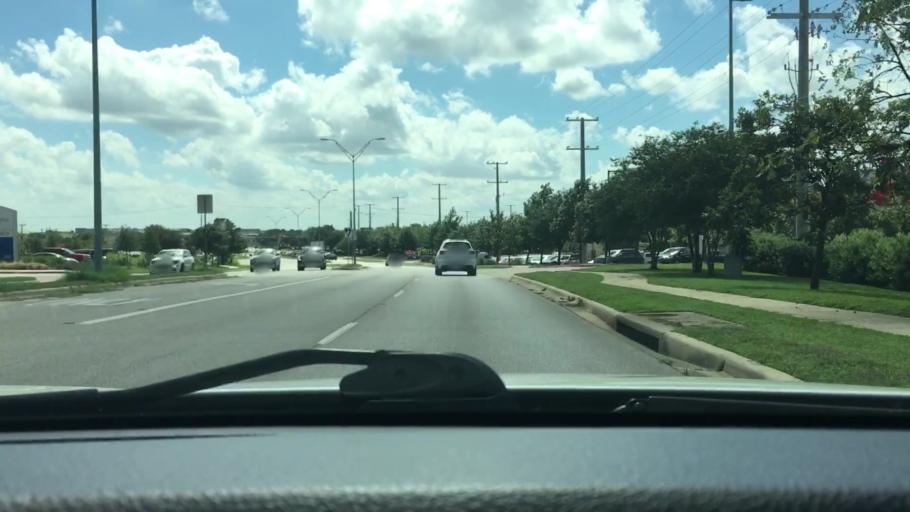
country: US
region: Texas
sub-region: Williamson County
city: Round Rock
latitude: 30.5627
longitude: -97.6874
